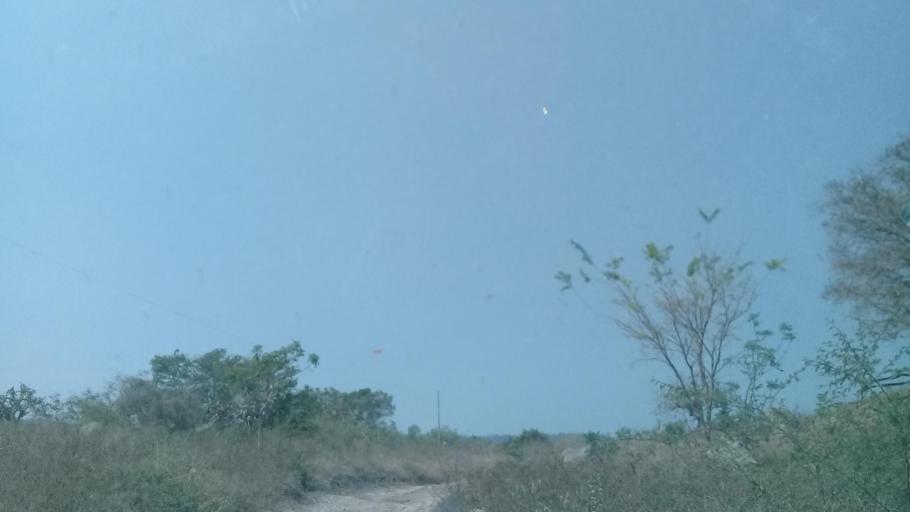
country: MX
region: Veracruz
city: El Castillo
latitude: 19.5695
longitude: -96.8059
